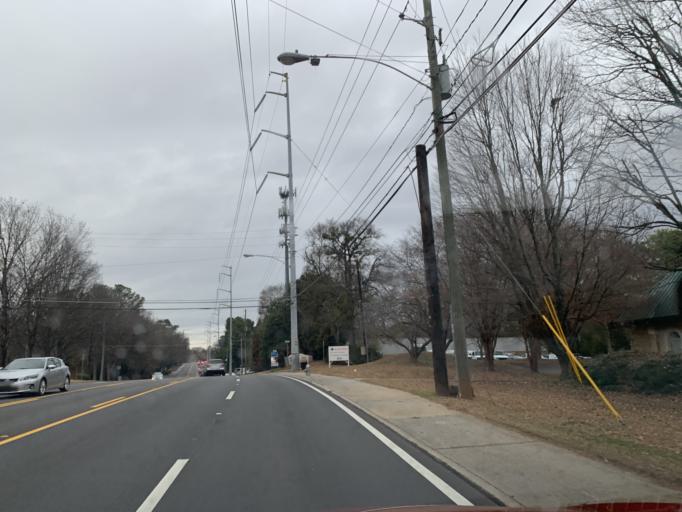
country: US
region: Georgia
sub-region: Fulton County
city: Sandy Springs
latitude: 33.8923
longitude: -84.3811
